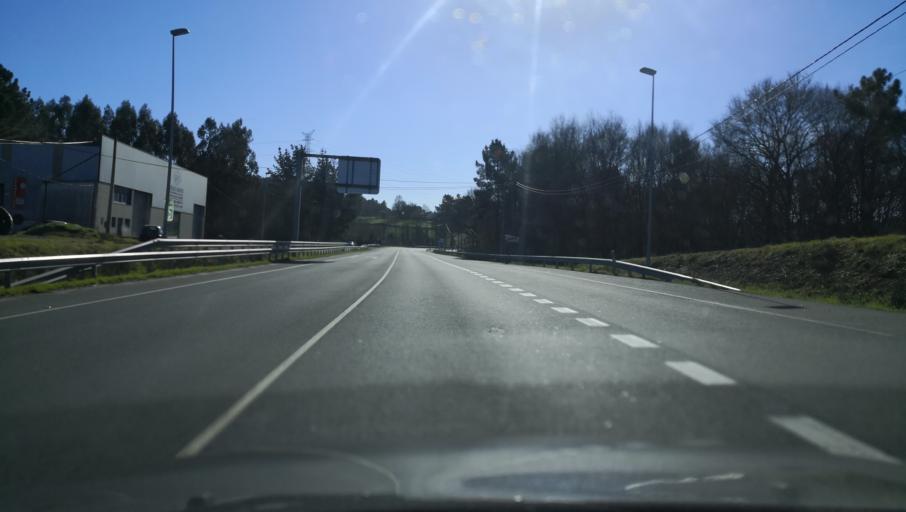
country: ES
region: Galicia
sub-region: Provincia de Pontevedra
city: Silleda
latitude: 42.7171
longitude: -8.2824
